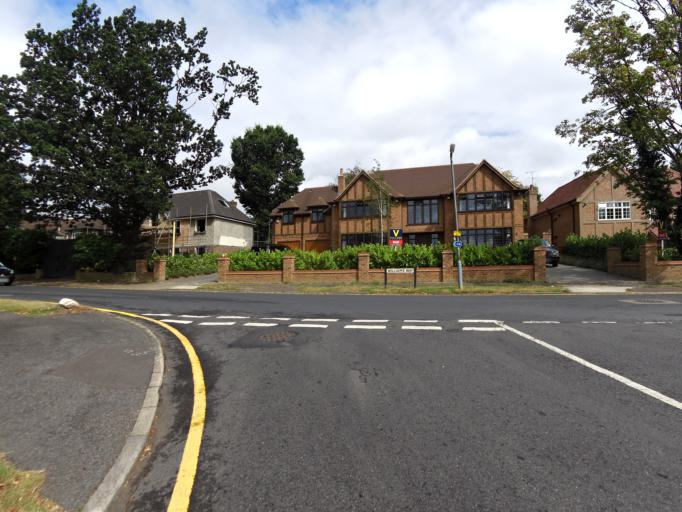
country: GB
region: England
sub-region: Hertfordshire
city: Radlett
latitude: 51.6852
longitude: -0.3093
